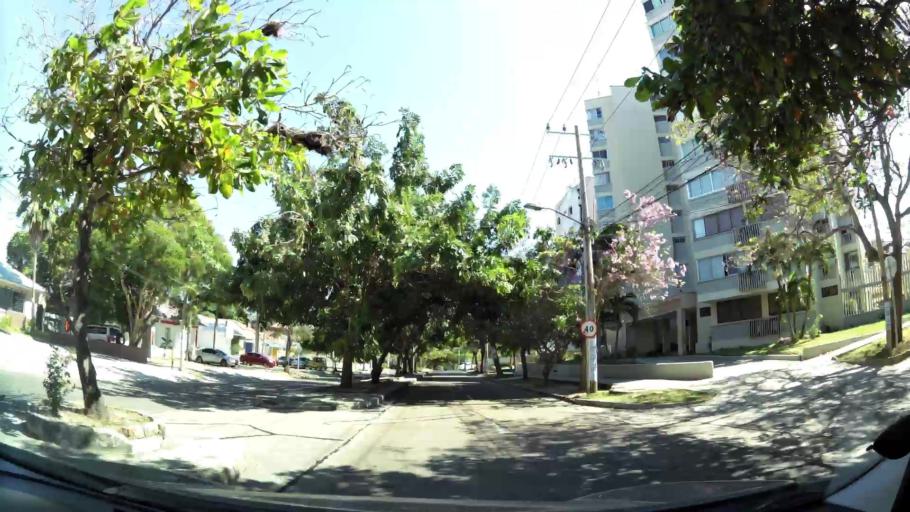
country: CO
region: Atlantico
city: Barranquilla
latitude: 10.9979
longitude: -74.7960
